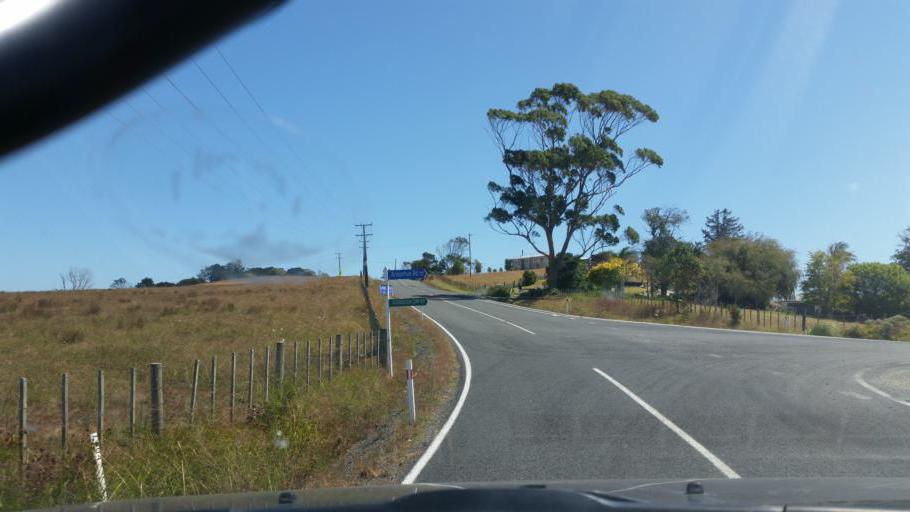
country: NZ
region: Northland
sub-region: Kaipara District
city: Dargaville
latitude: -36.0063
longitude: 173.9481
